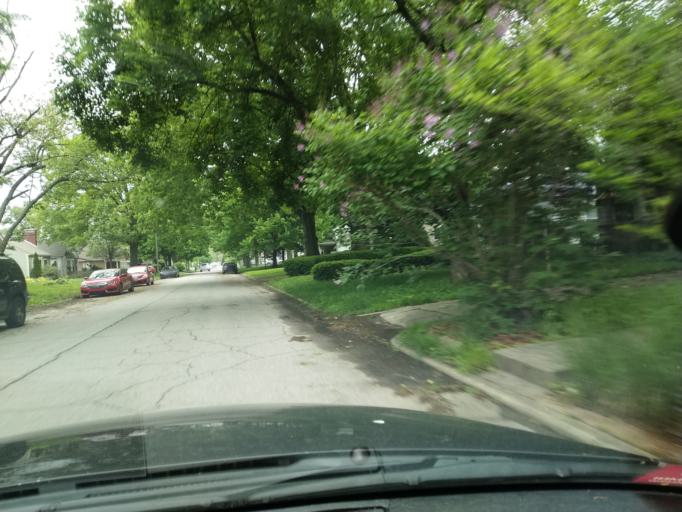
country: US
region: Indiana
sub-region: Marion County
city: Broad Ripple
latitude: 39.8454
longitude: -86.1278
